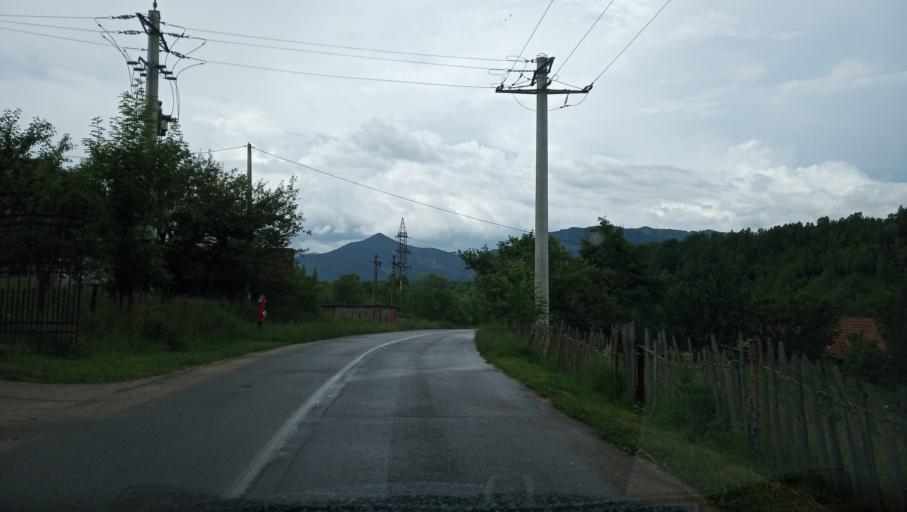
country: RO
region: Hunedoara
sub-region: Oras Petrila
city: Petrila
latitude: 45.4180
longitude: 23.4094
